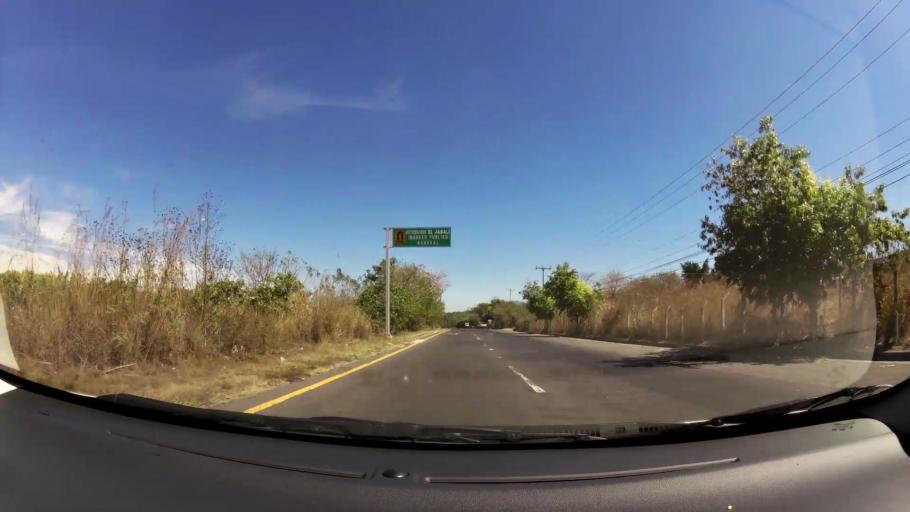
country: SV
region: La Libertad
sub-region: Distrito de Quezaltepeque
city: Quezaltepeque
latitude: 13.8074
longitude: -89.3244
